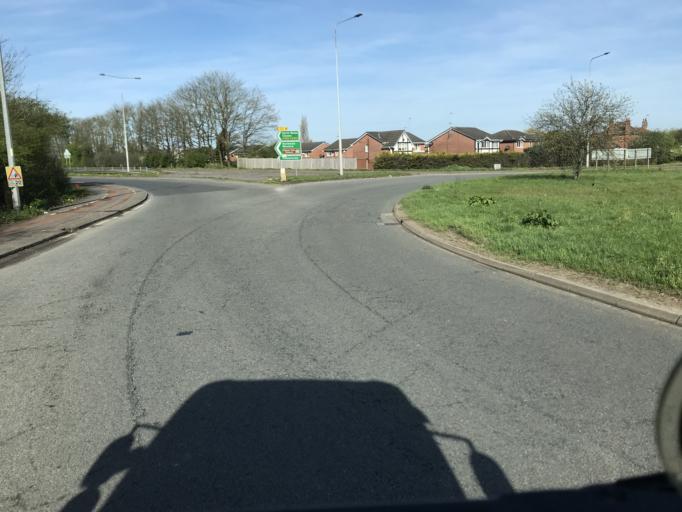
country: GB
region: England
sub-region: Cheshire West and Chester
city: Marston
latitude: 53.2500
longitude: -2.4733
